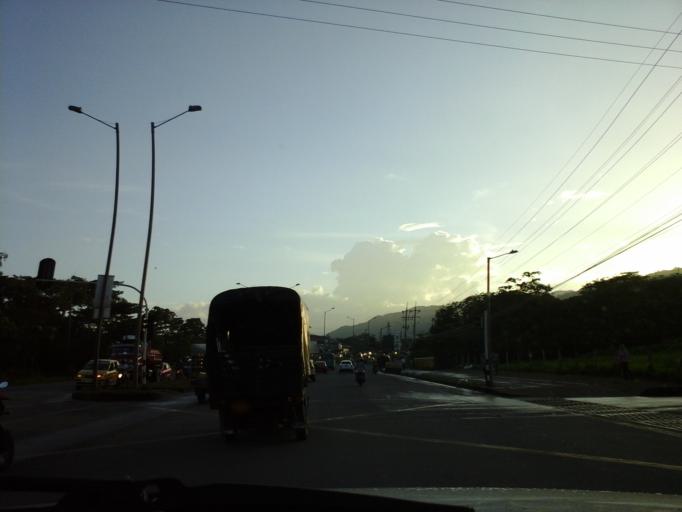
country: CO
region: Meta
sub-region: Villavicencio
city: Villavicencio
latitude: 4.1156
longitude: -73.6300
